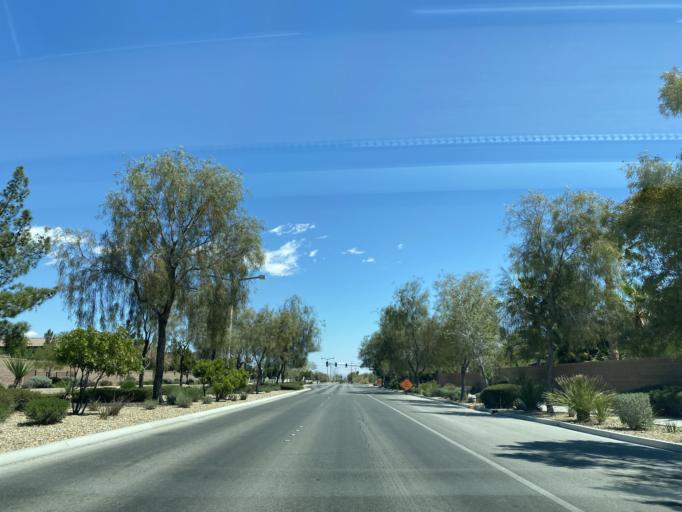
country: US
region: Nevada
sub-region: Clark County
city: North Las Vegas
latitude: 36.3053
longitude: -115.2175
